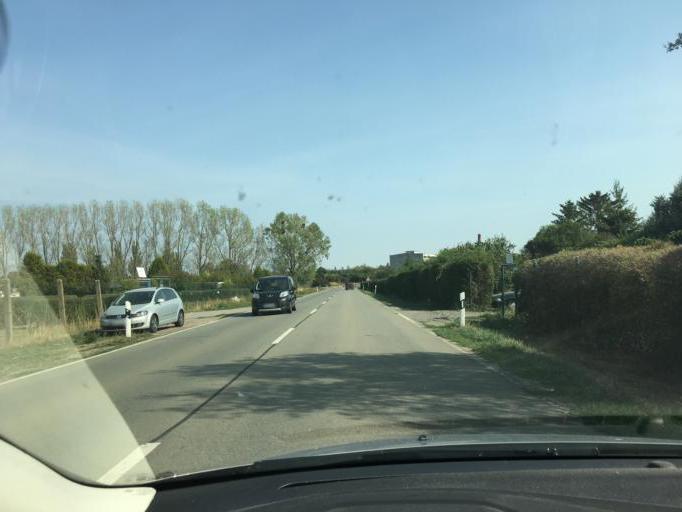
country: DE
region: Saxony-Anhalt
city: Barby
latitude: 51.9779
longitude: 11.8725
